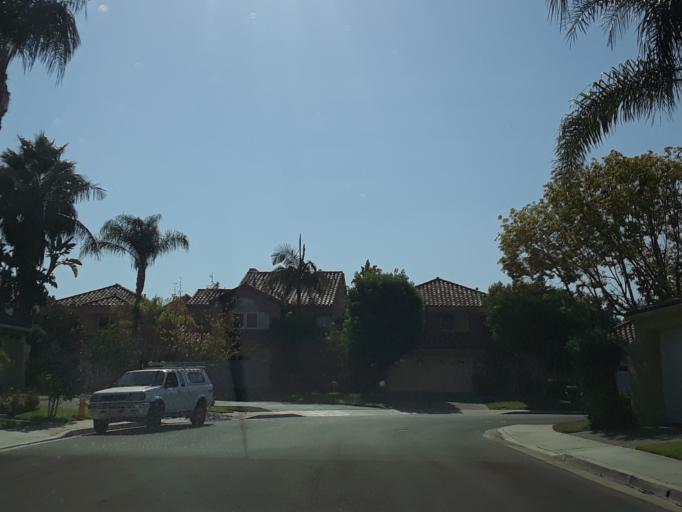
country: US
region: California
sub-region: Orange County
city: Irvine
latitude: 33.6798
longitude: -117.8226
